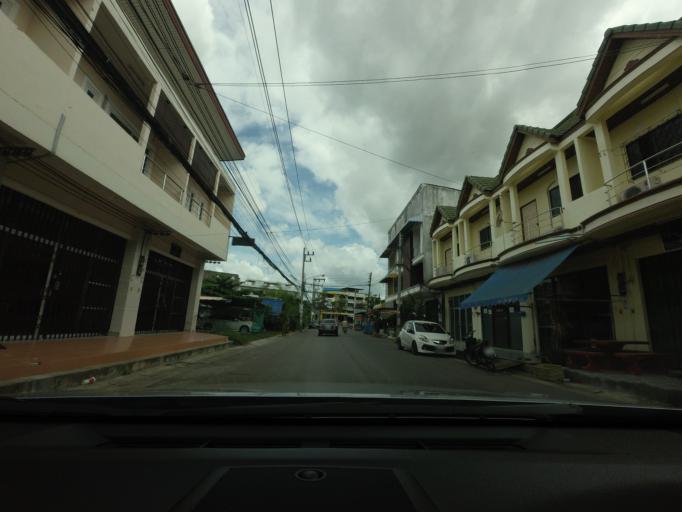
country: TH
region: Songkhla
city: Hat Yai
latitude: 7.0132
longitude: 100.4577
